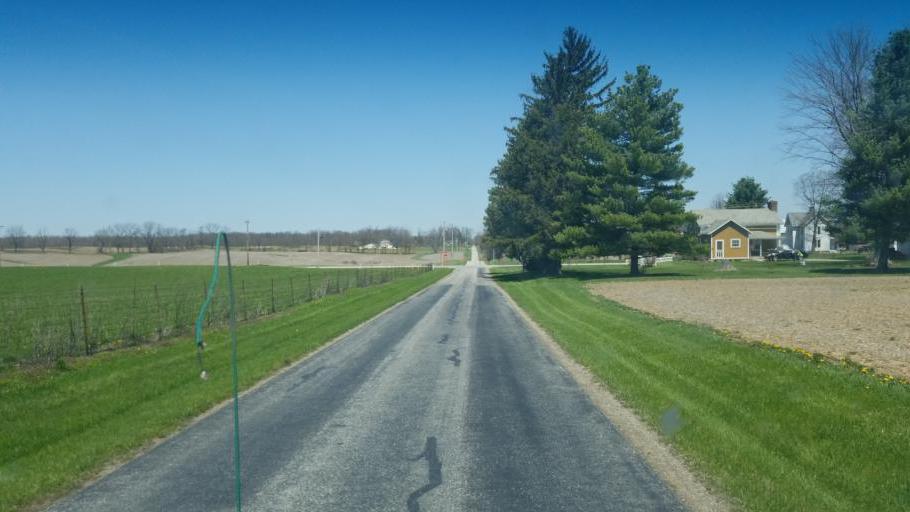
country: US
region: Ohio
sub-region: Huron County
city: New London
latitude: 41.0869
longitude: -82.4379
